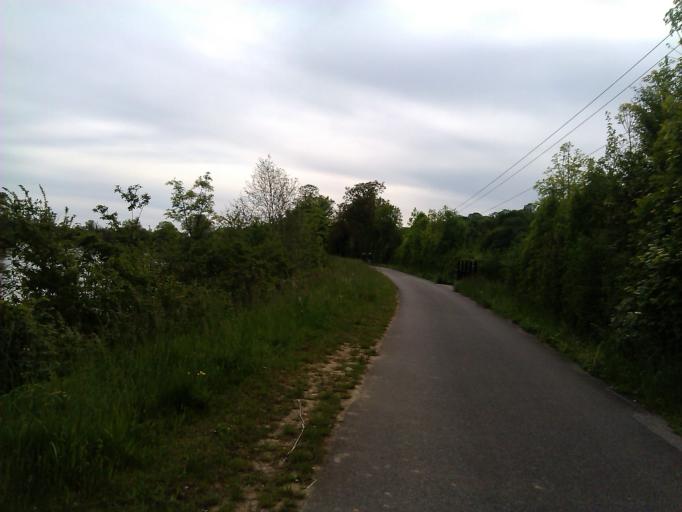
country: FR
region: Franche-Comte
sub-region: Departement du Doubs
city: Saint-Vit
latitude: 47.1735
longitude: 5.7885
